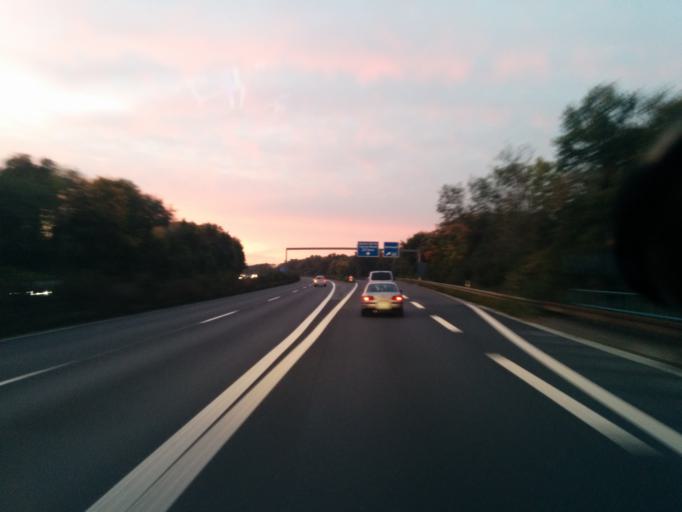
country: DE
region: North Rhine-Westphalia
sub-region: Regierungsbezirk Arnsberg
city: Bochum
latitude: 51.4924
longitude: 7.2756
